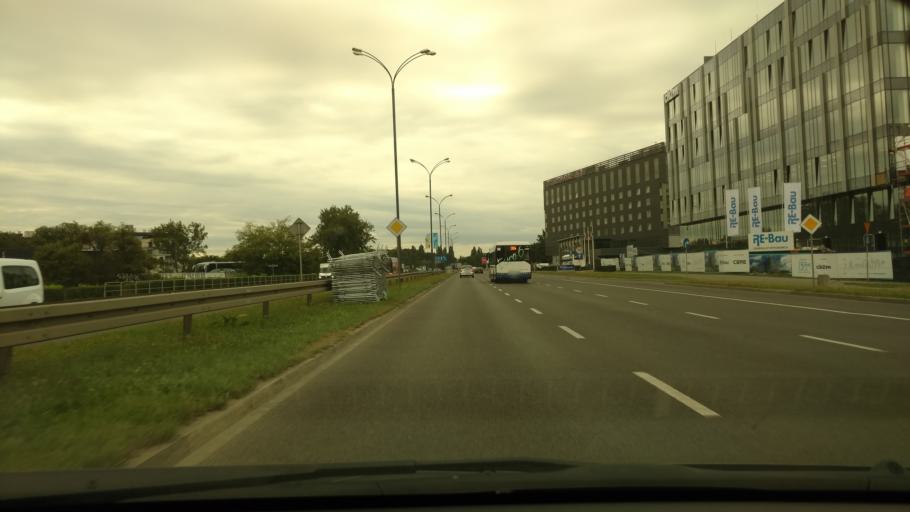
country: PL
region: Lesser Poland Voivodeship
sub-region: Krakow
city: Krakow
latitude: 50.0460
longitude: 19.9342
